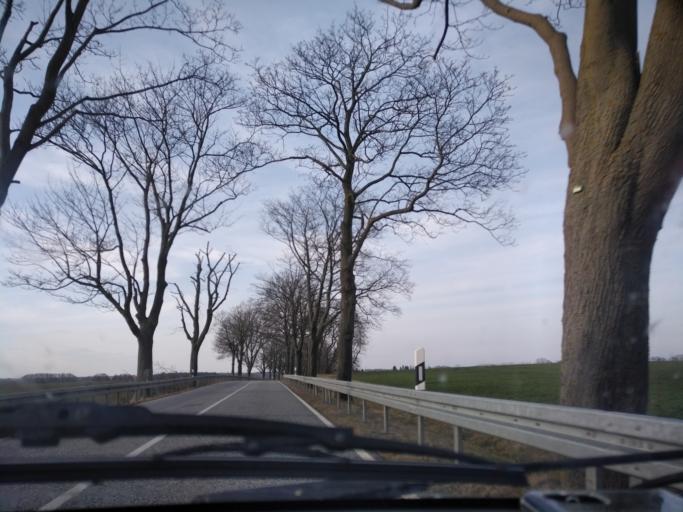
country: DE
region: Brandenburg
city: Juterbog
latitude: 51.9687
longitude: 13.1069
